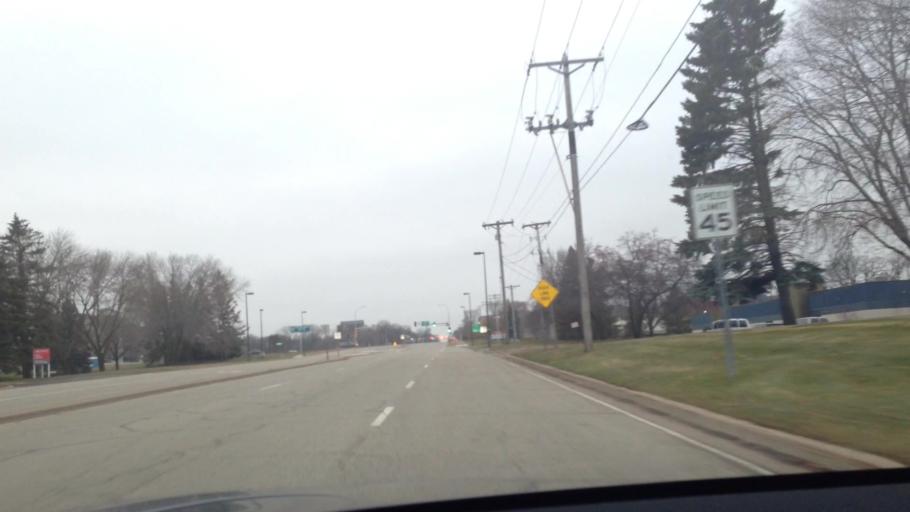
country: US
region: Minnesota
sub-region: Dakota County
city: Mendota Heights
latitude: 44.8653
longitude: -93.1673
